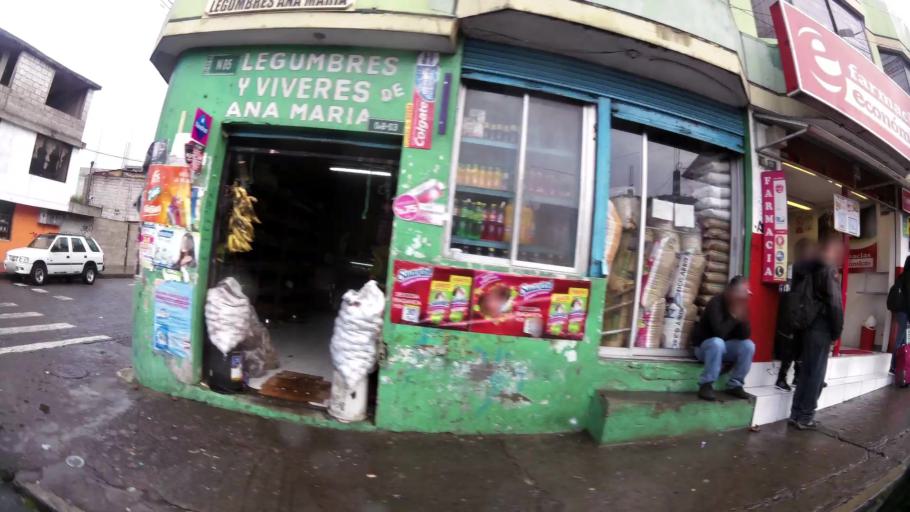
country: EC
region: Pichincha
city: Quito
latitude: -0.0848
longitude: -78.5059
